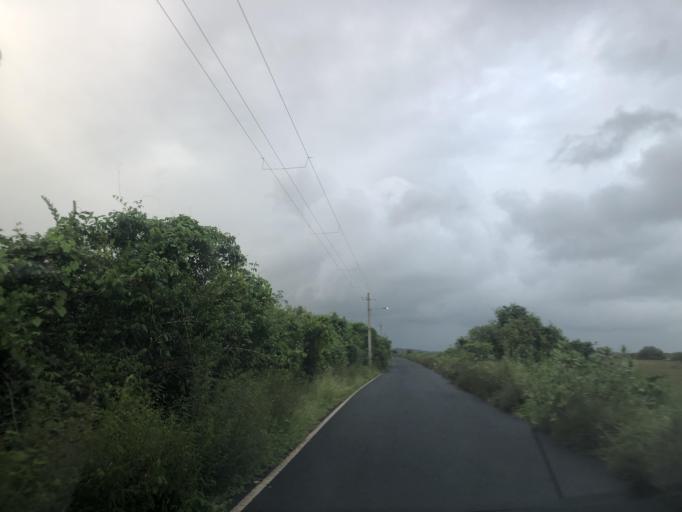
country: IN
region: Goa
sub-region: North Goa
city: Serula
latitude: 15.5124
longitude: 73.8872
